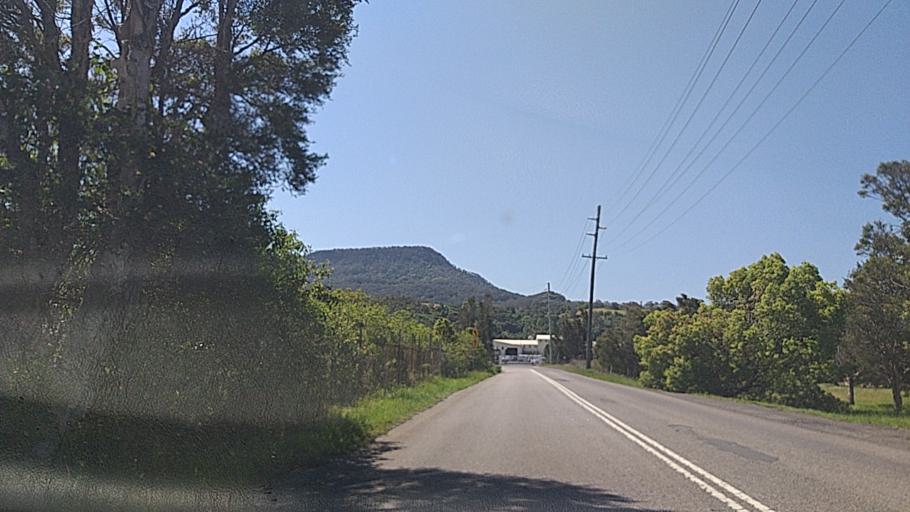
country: AU
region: New South Wales
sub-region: Wollongong
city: Koonawarra
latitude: -34.4700
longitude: 150.8066
